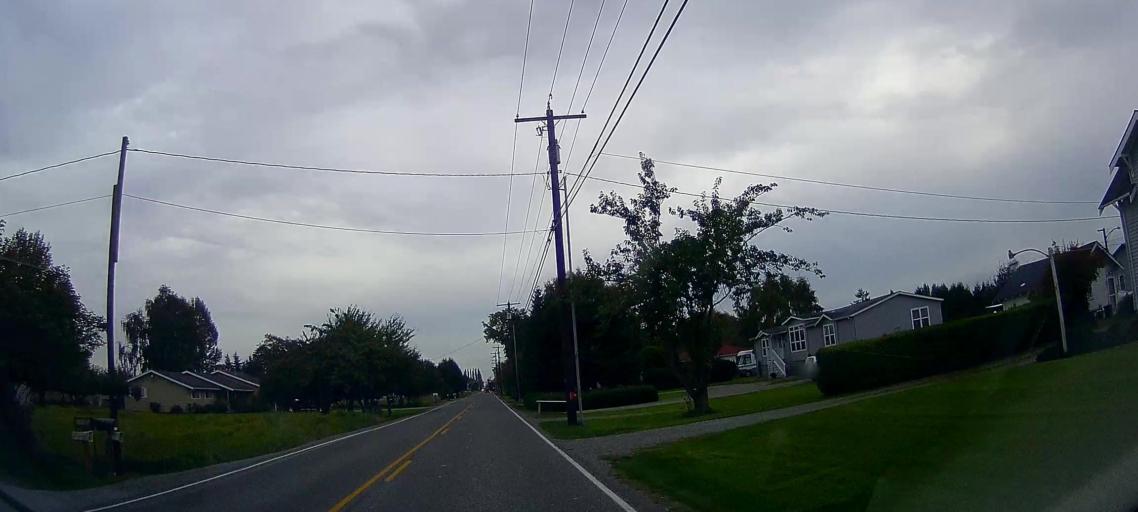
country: US
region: Washington
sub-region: Skagit County
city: Mount Vernon
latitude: 48.4398
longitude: -122.3788
